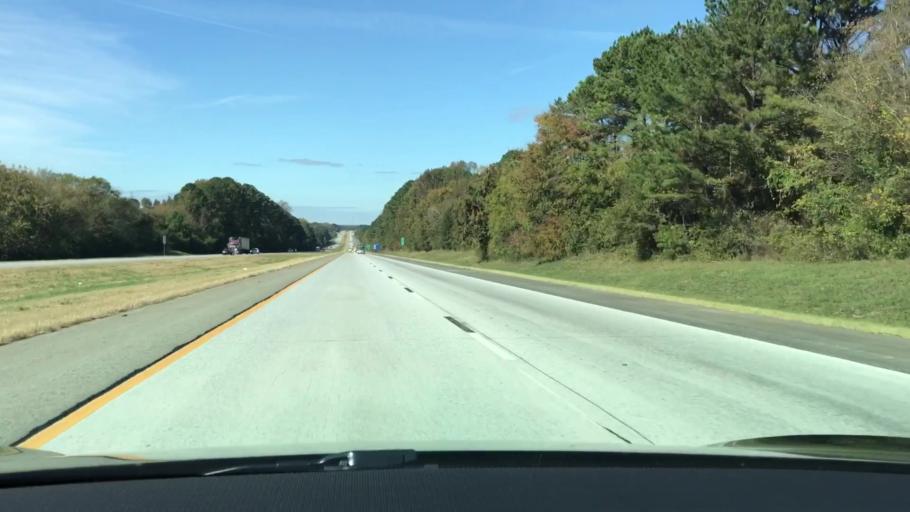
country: US
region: Georgia
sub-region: Putnam County
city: Jefferson
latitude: 33.5432
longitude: -83.3266
